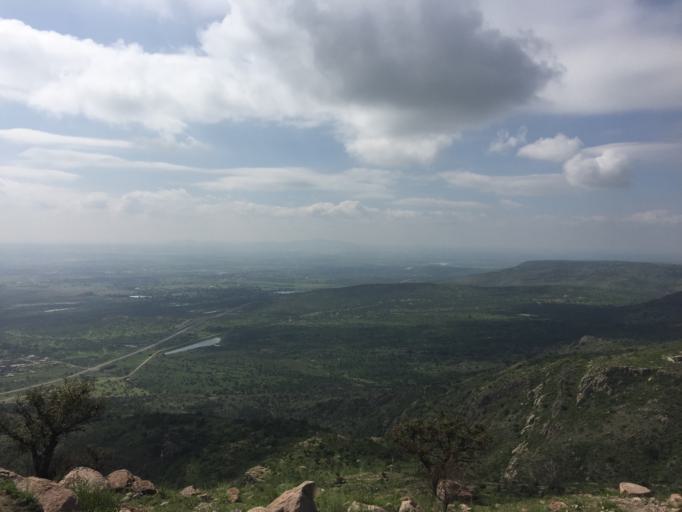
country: MX
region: Aguascalientes
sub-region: Aguascalientes
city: La Loma de los Negritos
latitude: 21.8841
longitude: -102.4174
